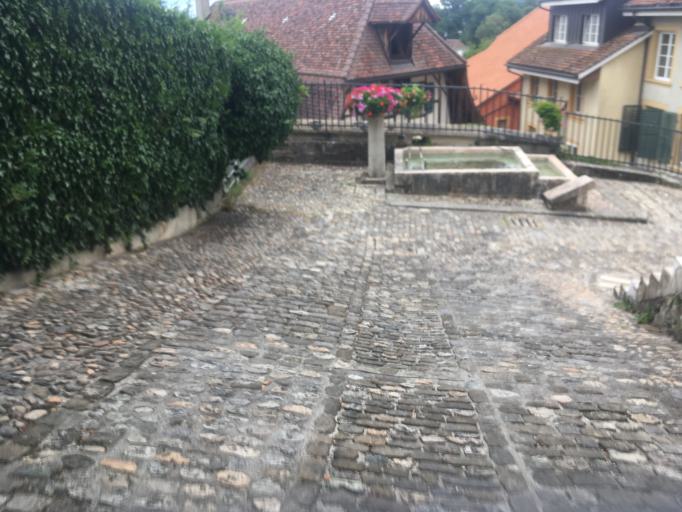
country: CH
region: Bern
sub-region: Seeland District
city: Erlach
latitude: 47.0449
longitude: 7.0960
